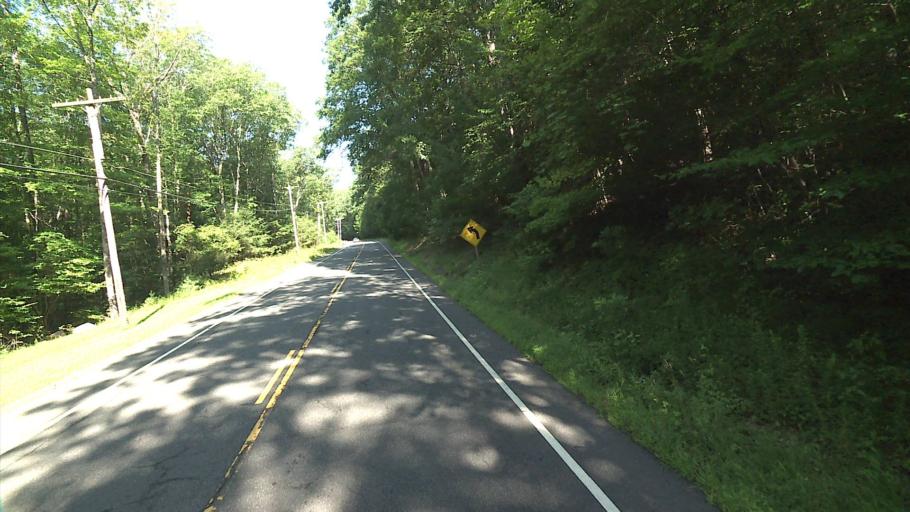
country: US
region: Connecticut
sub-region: Hartford County
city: North Granby
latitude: 41.9744
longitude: -72.8768
